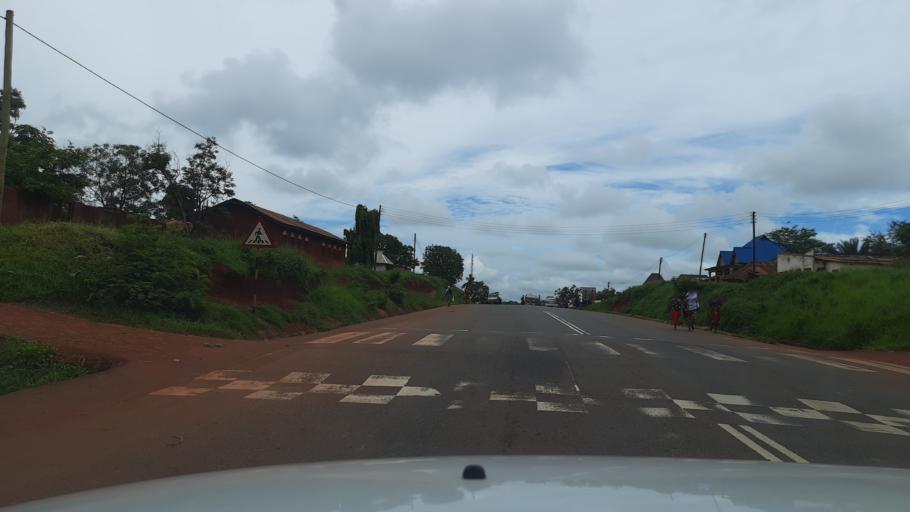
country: TZ
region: Pwani
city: Lugoba
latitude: -6.0822
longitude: 38.2436
